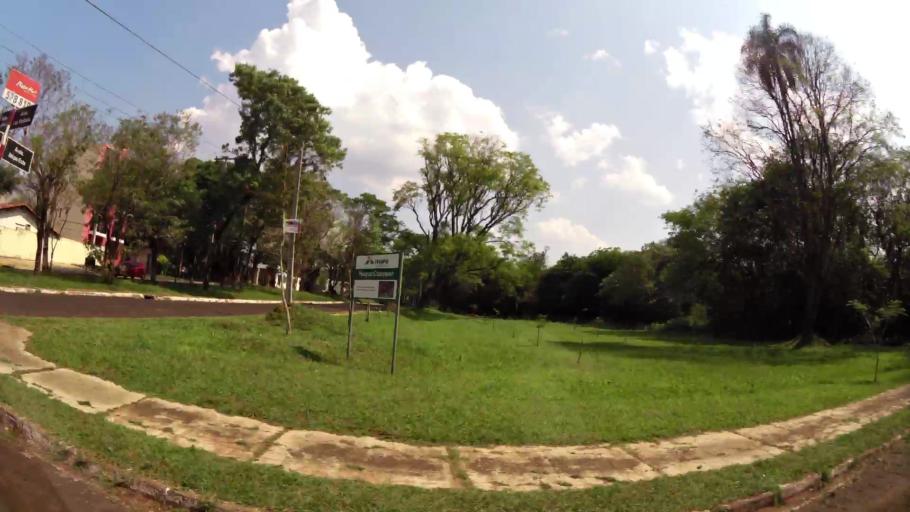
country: PY
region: Alto Parana
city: Ciudad del Este
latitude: -25.5156
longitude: -54.6310
